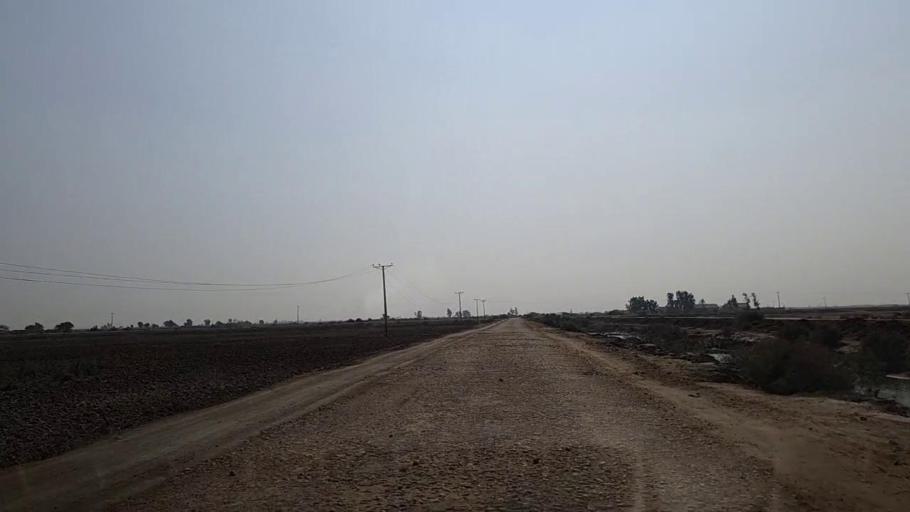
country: PK
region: Sindh
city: Thatta
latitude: 24.7140
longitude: 67.7684
